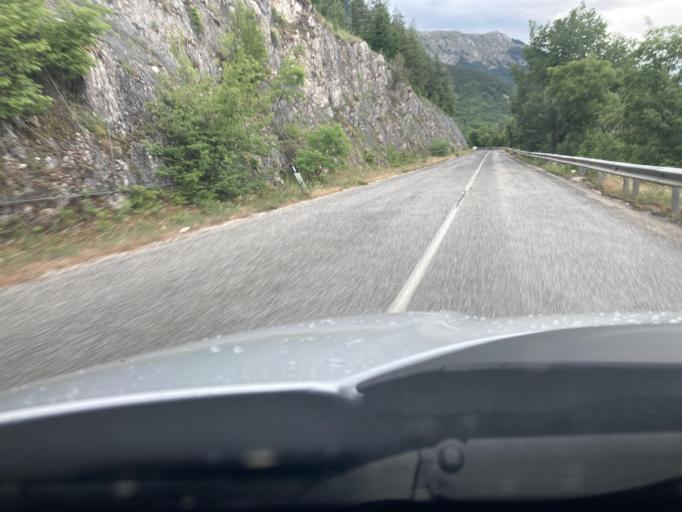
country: IT
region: Abruzzo
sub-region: Provincia dell' Aquila
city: San Panfilo d'Ocre
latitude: 42.2773
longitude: 13.4720
